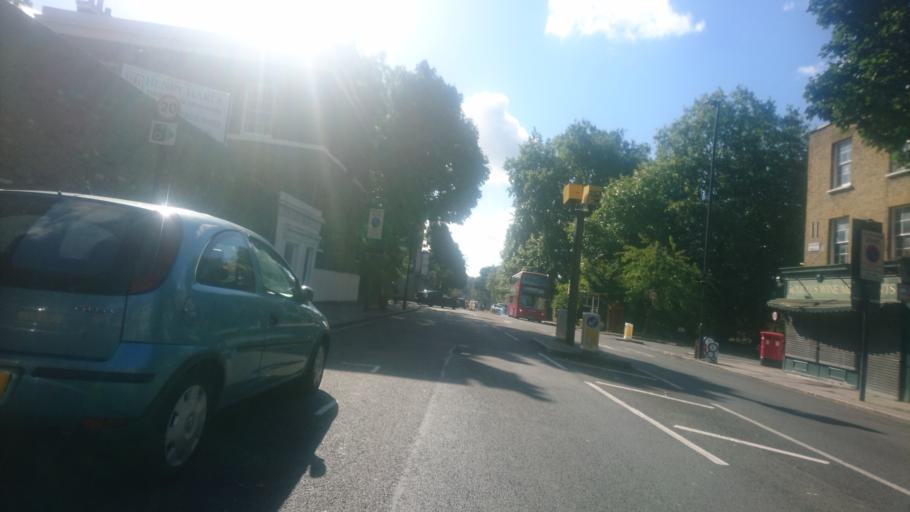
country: GB
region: England
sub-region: Greater London
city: Islington
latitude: 51.5422
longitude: -0.0987
